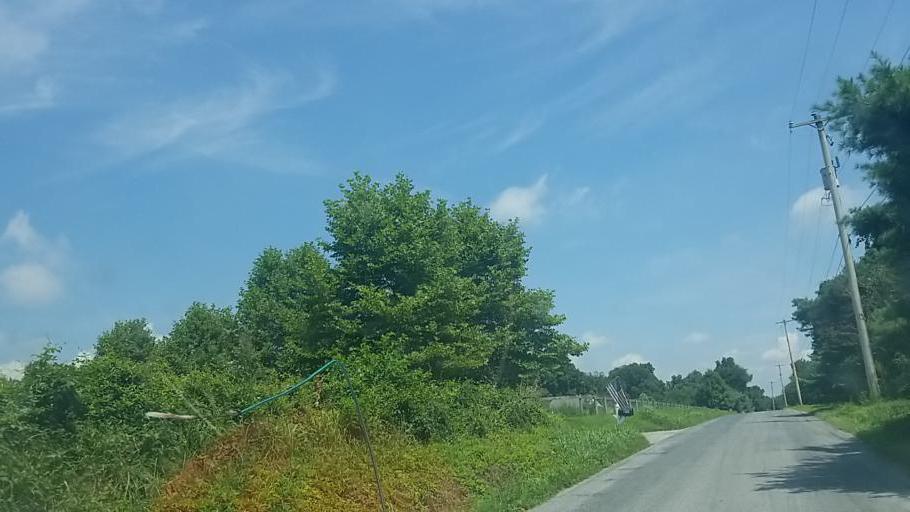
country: US
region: Pennsylvania
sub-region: Chester County
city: Atglen
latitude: 39.8786
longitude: -75.9727
